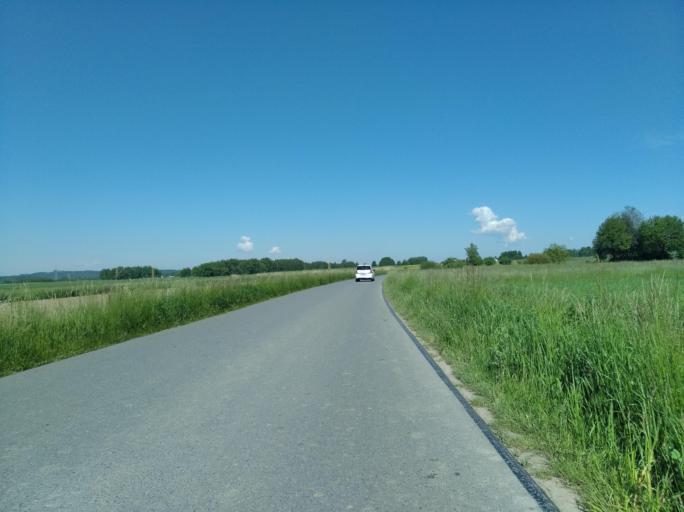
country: PL
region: Subcarpathian Voivodeship
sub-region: Powiat krosnienski
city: Odrzykon
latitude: 49.7277
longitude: 21.7553
